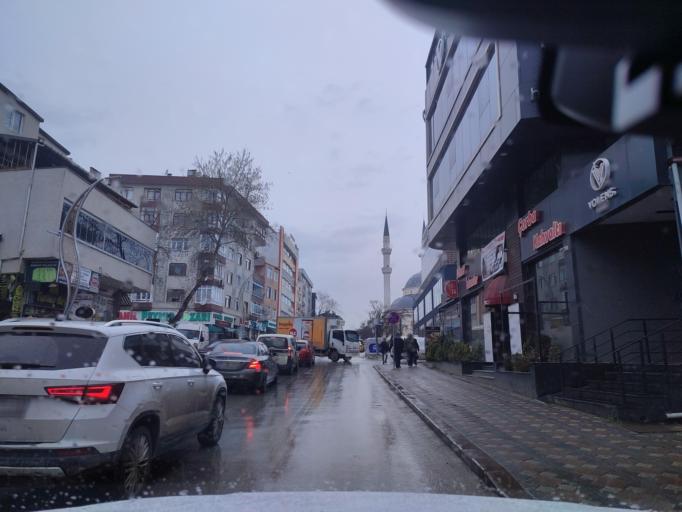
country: TR
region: Kocaeli
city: Gebze
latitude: 40.7982
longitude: 29.4404
